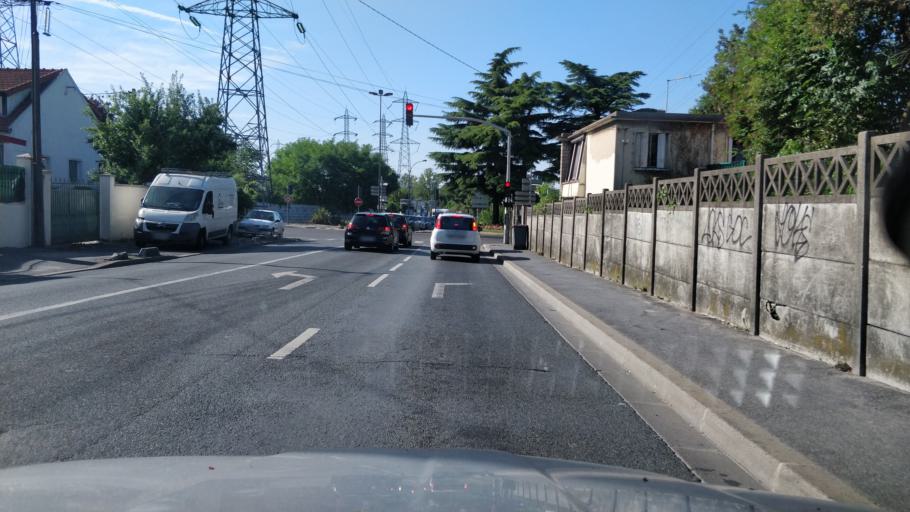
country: FR
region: Ile-de-France
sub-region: Departement de Seine-Saint-Denis
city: Villemomble
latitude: 48.8808
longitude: 2.4956
